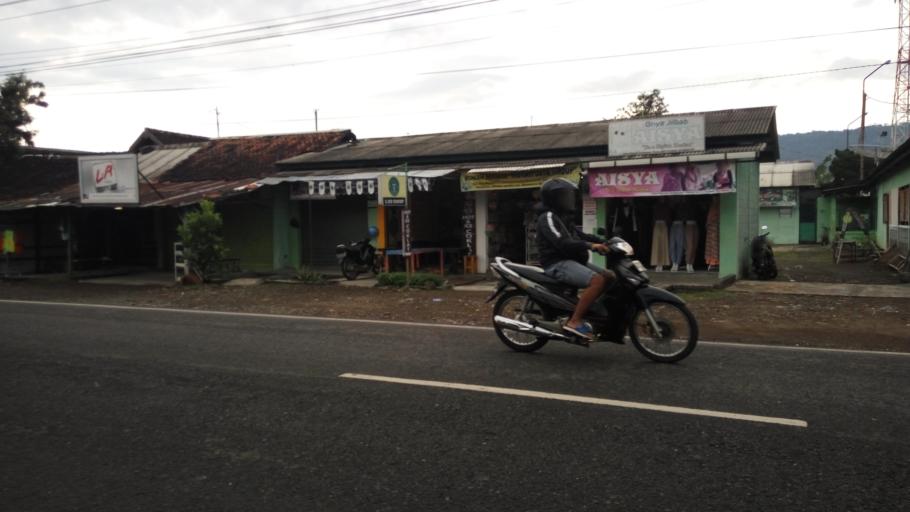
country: ID
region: Central Java
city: Ambarawa
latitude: -7.2671
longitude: 110.4039
